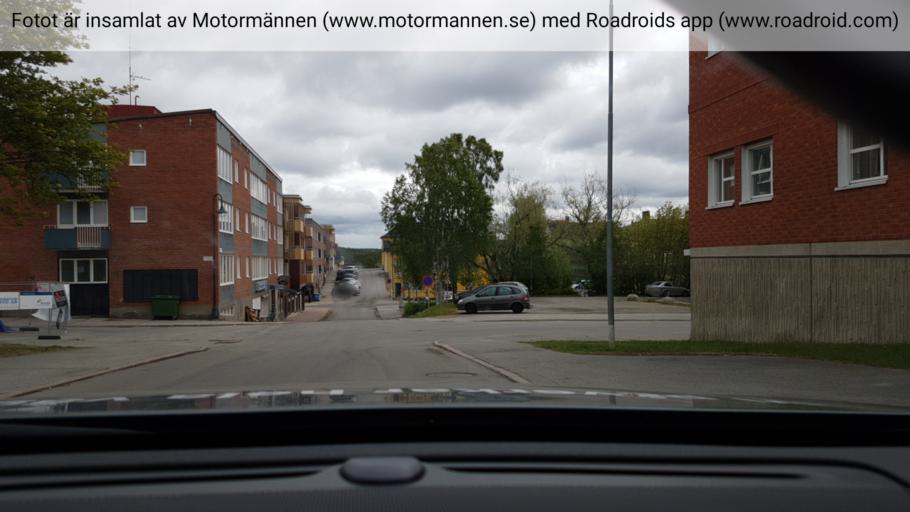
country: SE
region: Vaesterbotten
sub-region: Lycksele Kommun
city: Lycksele
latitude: 64.5960
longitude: 18.6732
